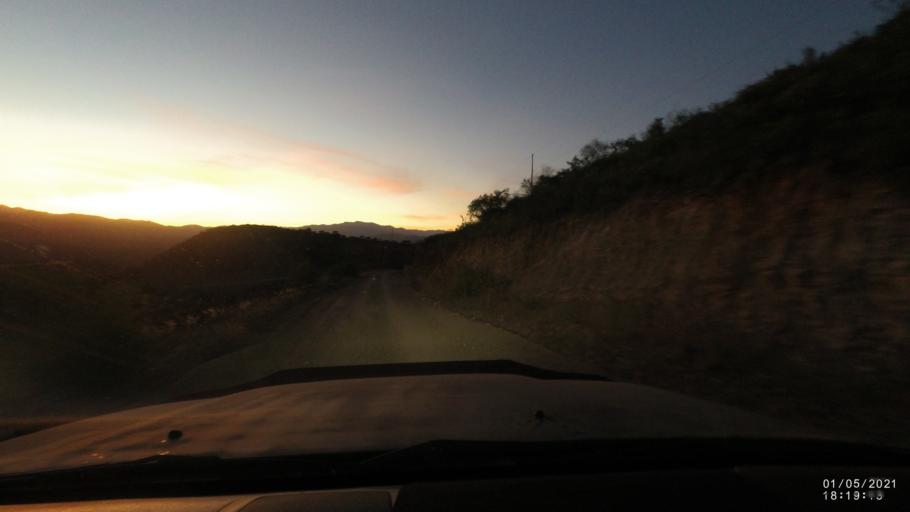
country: BO
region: Cochabamba
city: Capinota
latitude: -17.6631
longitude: -66.2240
